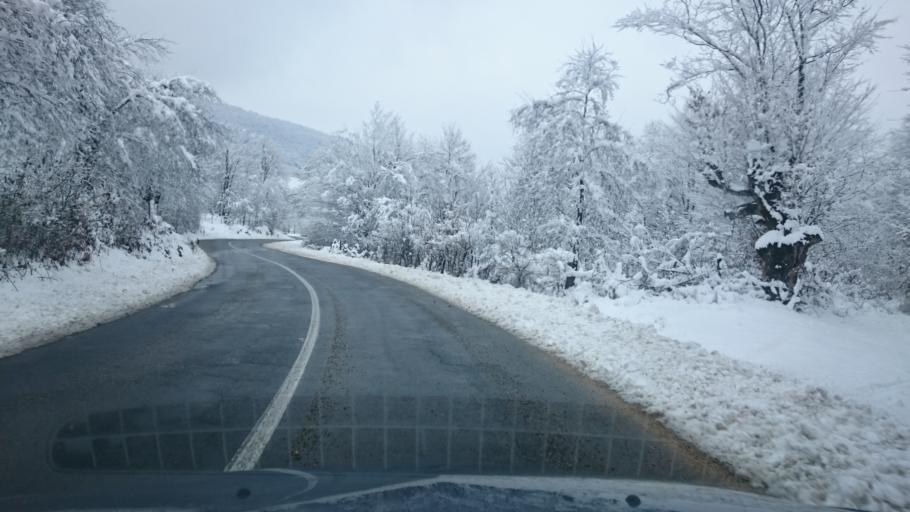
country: BA
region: Republika Srpska
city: Kotor-Varos
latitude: 44.6044
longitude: 17.2330
